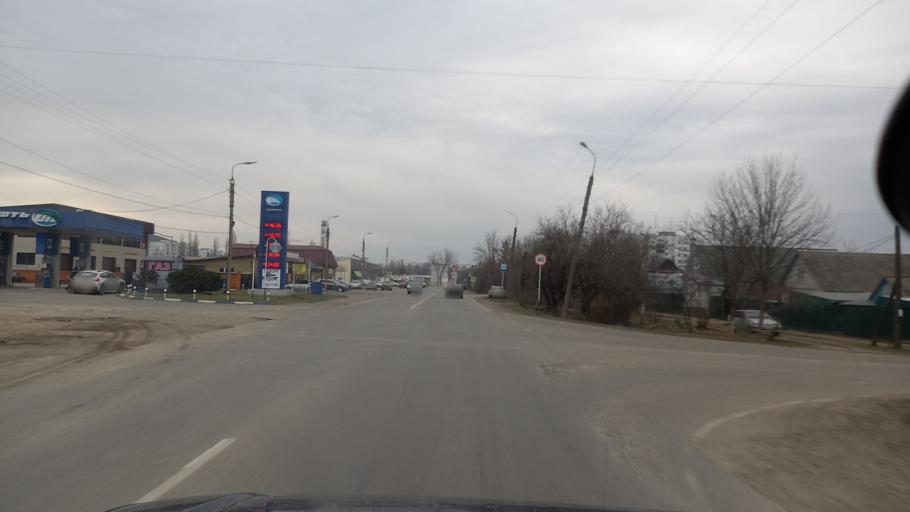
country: RU
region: Adygeya
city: Maykop
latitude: 44.5821
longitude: 40.1348
